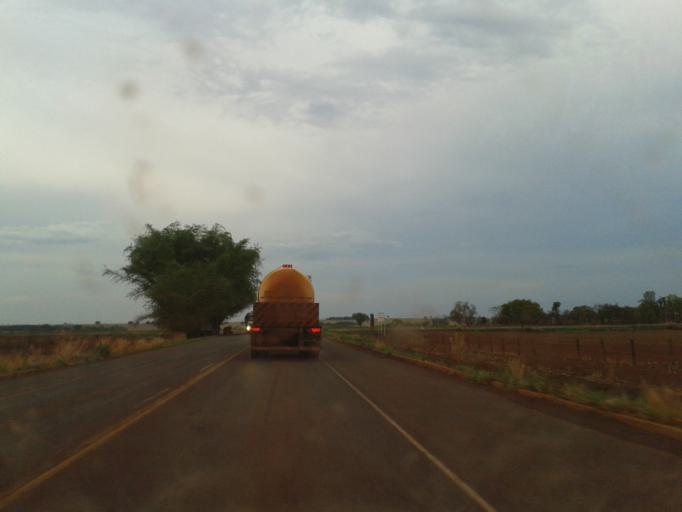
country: BR
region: Goias
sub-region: Santa Helena De Goias
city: Santa Helena de Goias
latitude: -17.9609
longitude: -50.4973
